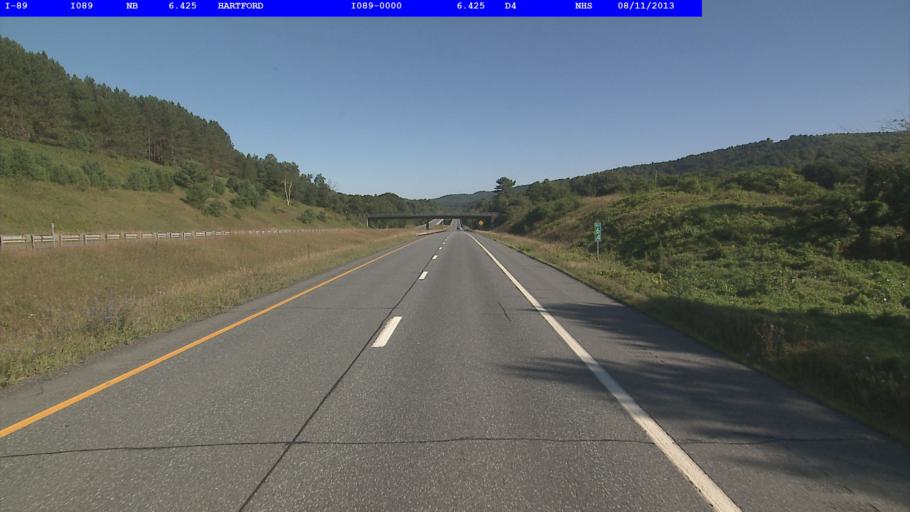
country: US
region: Vermont
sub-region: Windsor County
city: White River Junction
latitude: 43.6978
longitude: -72.4086
